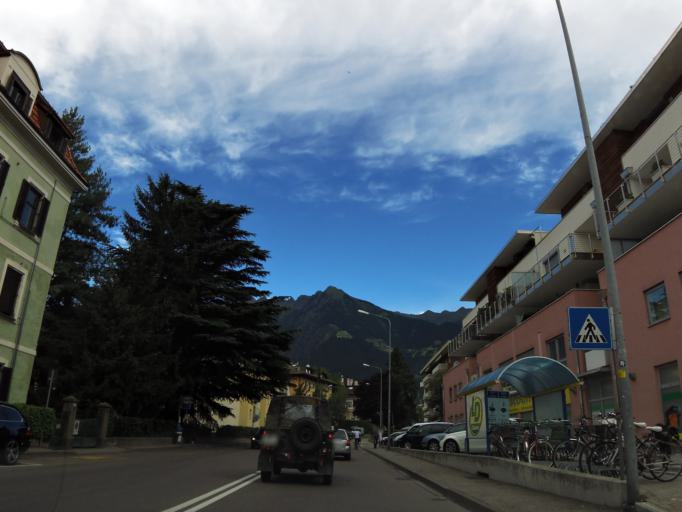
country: IT
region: Trentino-Alto Adige
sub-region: Bolzano
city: Merano
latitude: 46.6626
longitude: 11.1599
